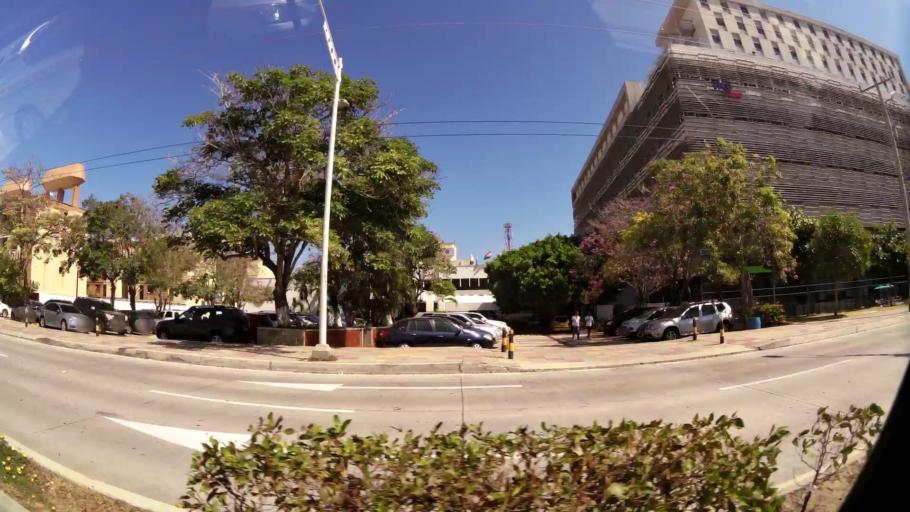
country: CO
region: Atlantico
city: Barranquilla
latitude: 11.0098
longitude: -74.8261
